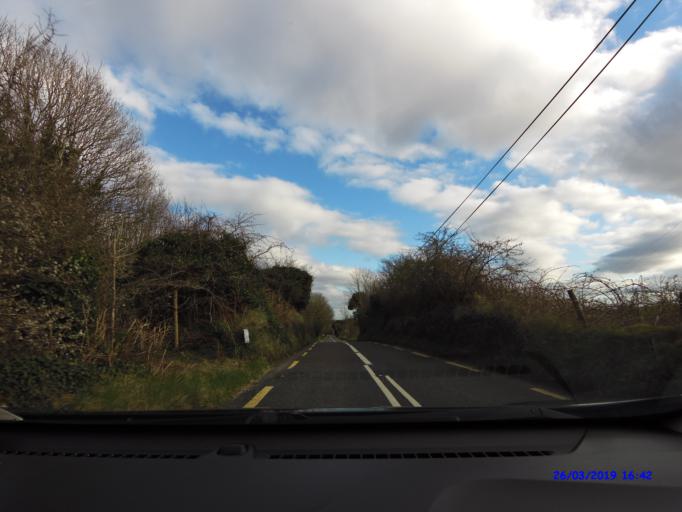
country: IE
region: Connaught
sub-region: Maigh Eo
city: Ballyhaunis
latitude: 53.8684
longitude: -8.7676
